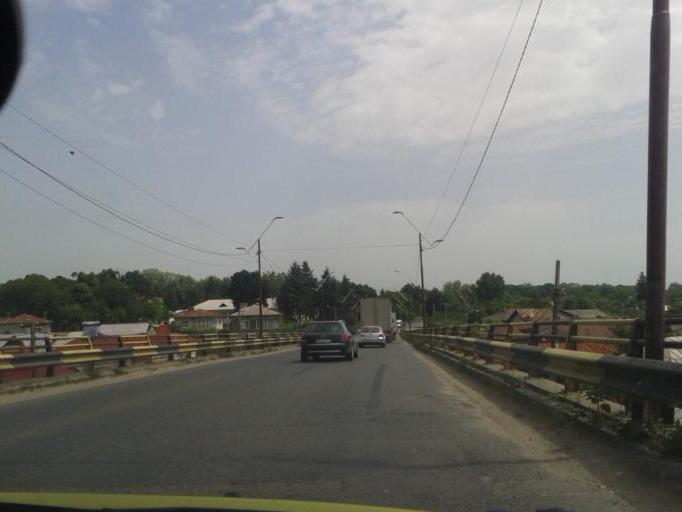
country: RO
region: Dambovita
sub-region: Oras Gaesti
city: Gaesti
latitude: 44.7137
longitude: 25.3102
